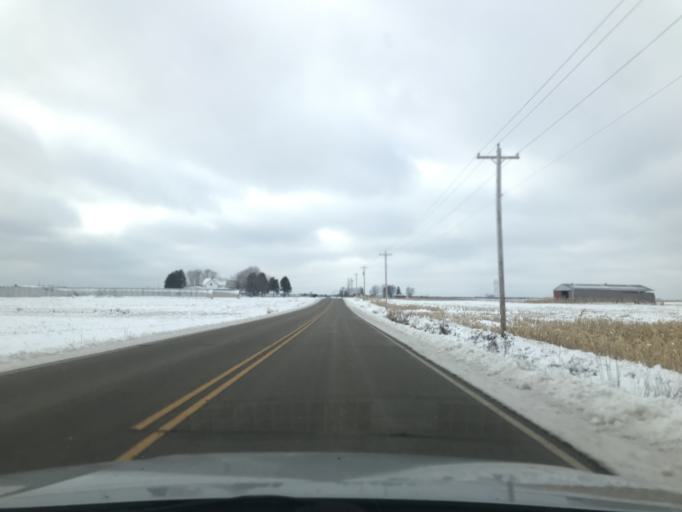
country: US
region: Wisconsin
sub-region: Oconto County
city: Oconto
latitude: 44.9498
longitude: -87.9214
